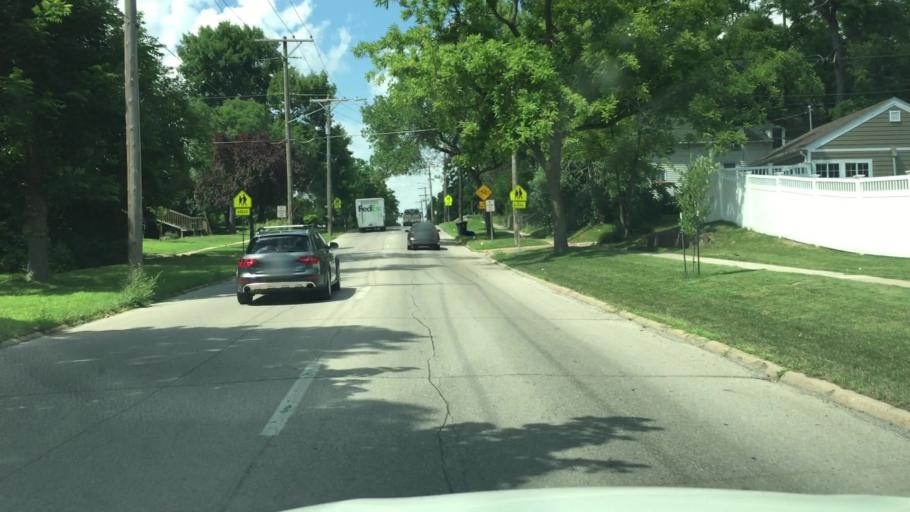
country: US
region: Iowa
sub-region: Johnson County
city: Iowa City
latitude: 41.6670
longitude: -91.5228
